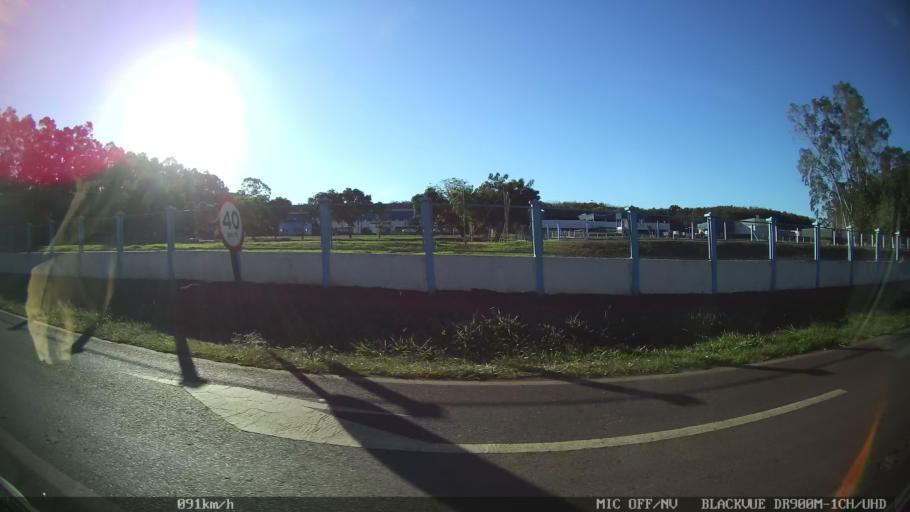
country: BR
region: Sao Paulo
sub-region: Guapiacu
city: Guapiacu
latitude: -20.7605
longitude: -49.1756
